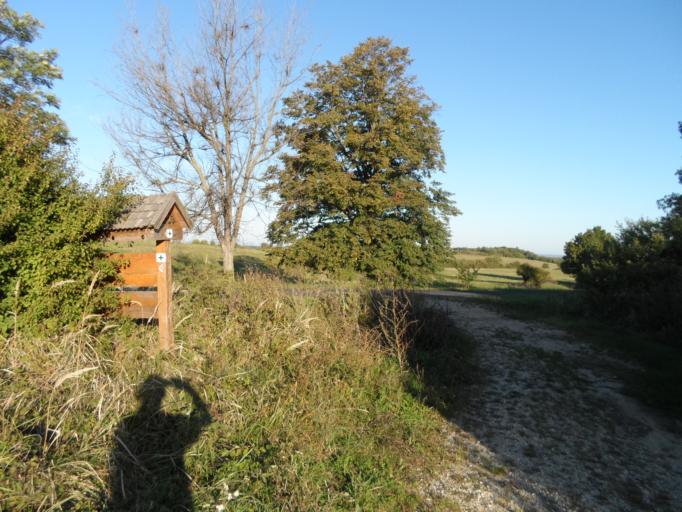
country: HU
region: Veszprem
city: Papa
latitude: 47.2423
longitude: 17.5374
